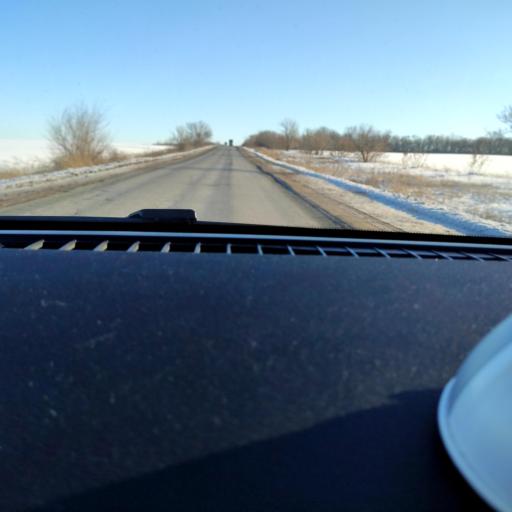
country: RU
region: Samara
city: Spiridonovka
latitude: 53.1445
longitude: 50.5590
